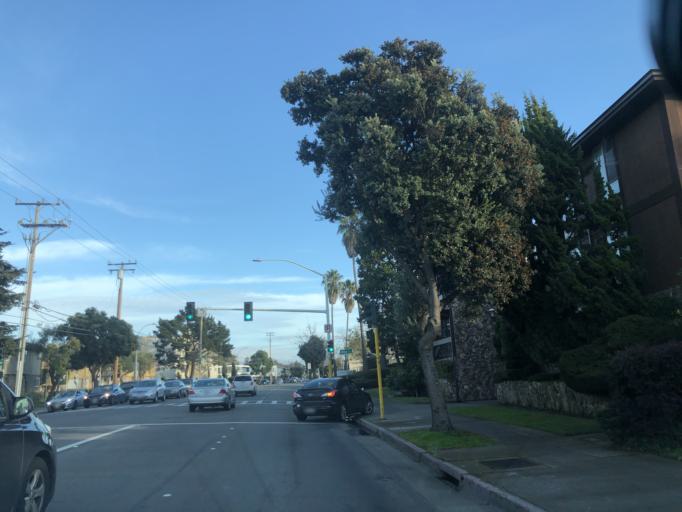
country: US
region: California
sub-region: Alameda County
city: Alameda
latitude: 37.7608
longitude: -122.2544
